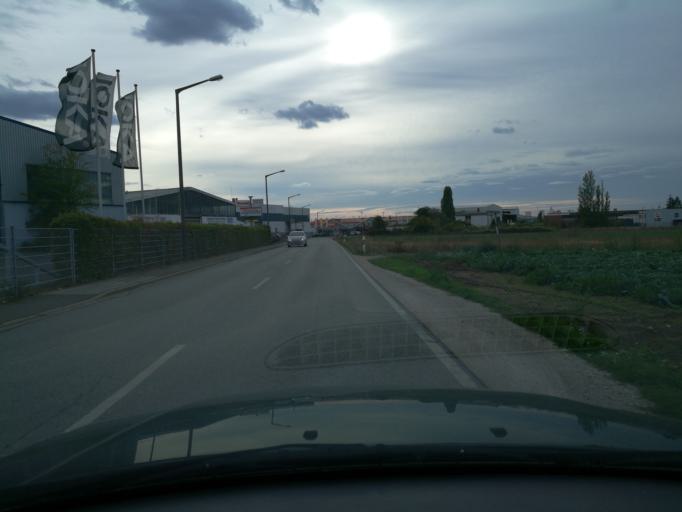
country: DE
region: Bavaria
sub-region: Regierungsbezirk Mittelfranken
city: Furth
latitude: 49.5128
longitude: 11.0091
